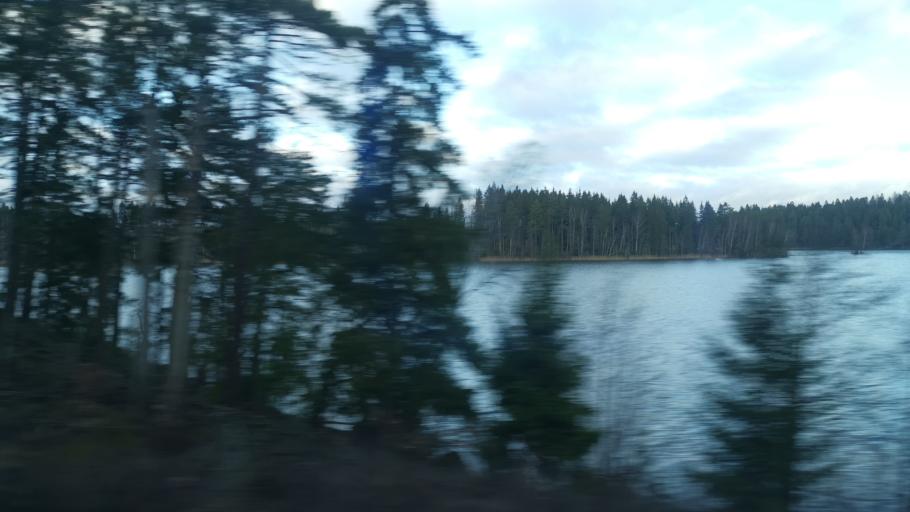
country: SE
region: Soedermanland
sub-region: Flens Kommun
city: Flen
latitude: 59.0415
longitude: 16.5355
